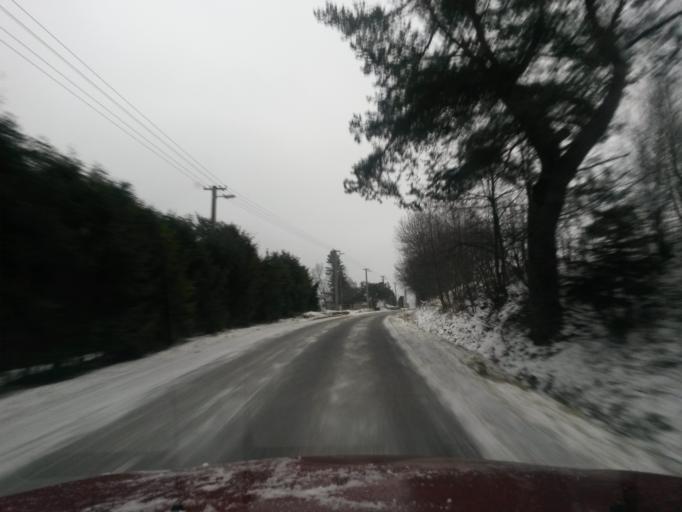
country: SK
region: Kosicky
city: Medzev
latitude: 48.7278
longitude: 20.7238
